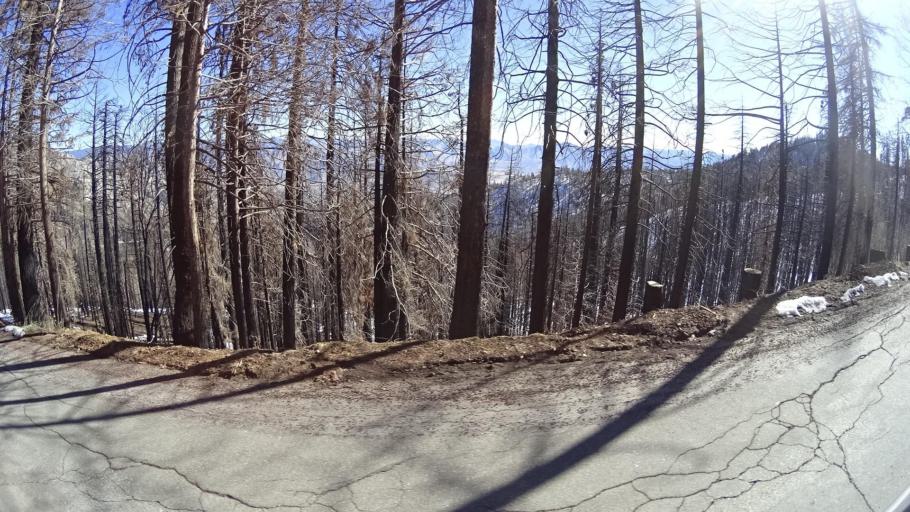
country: US
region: California
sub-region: Kern County
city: Alta Sierra
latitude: 35.7173
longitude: -118.5543
